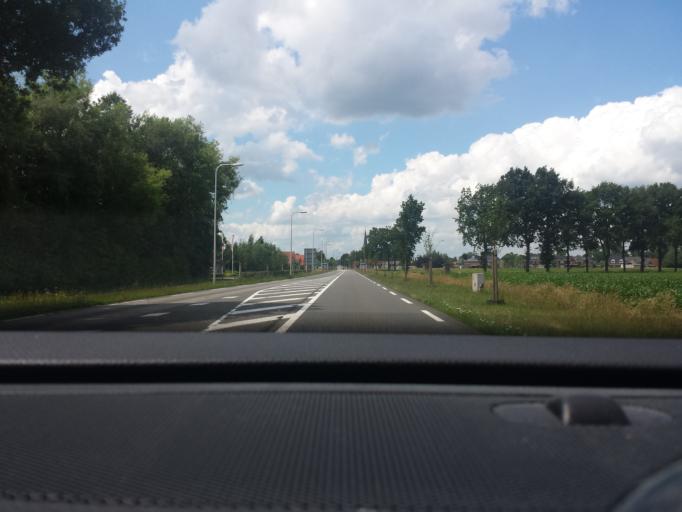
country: NL
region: Overijssel
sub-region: Gemeente Haaksbergen
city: Haaksbergen
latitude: 52.1733
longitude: 6.7073
